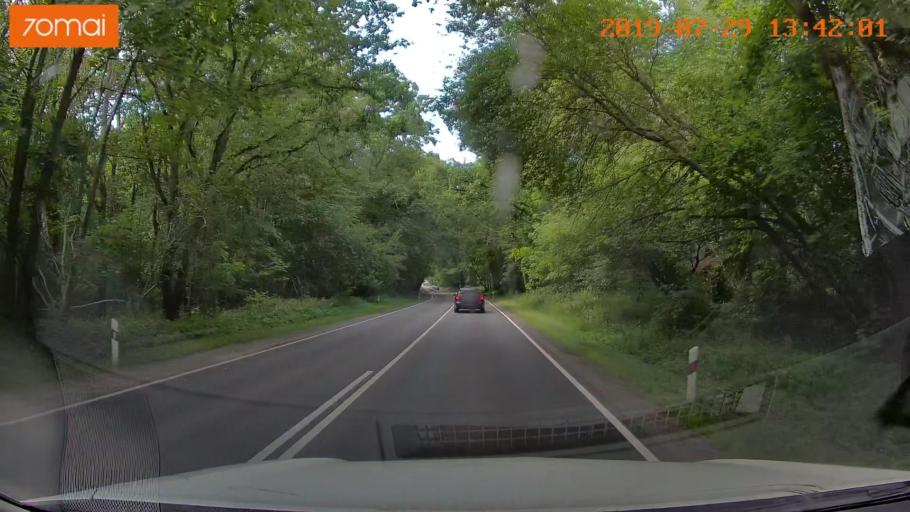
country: RU
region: Kaliningrad
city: Svetlyy
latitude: 54.7364
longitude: 20.1189
